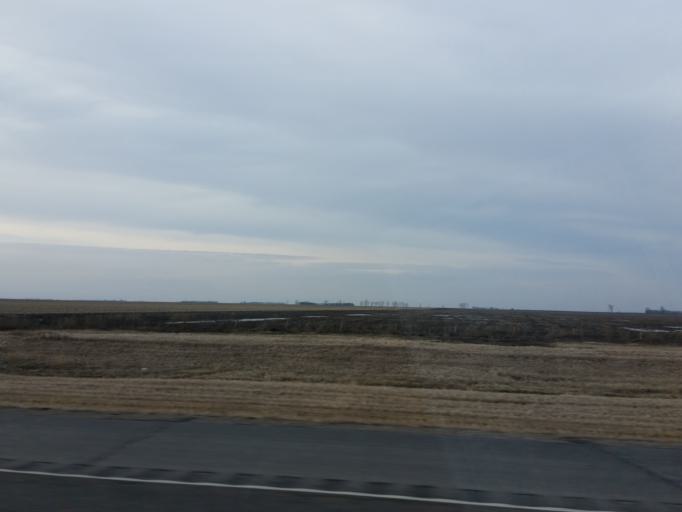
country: US
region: North Dakota
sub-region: Cass County
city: Casselton
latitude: 46.8768
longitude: -97.1154
